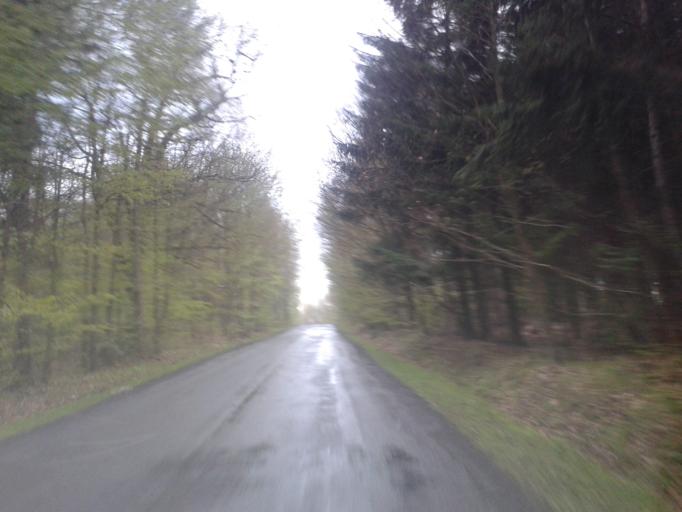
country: CZ
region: Central Bohemia
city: Hudlice
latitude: 49.9554
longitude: 13.9263
